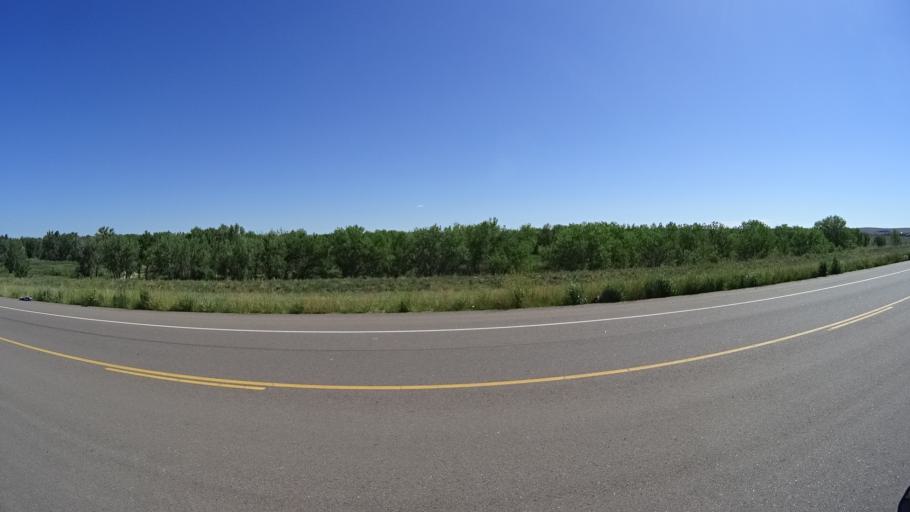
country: US
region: Colorado
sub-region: El Paso County
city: Security-Widefield
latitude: 38.7486
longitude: -104.6506
